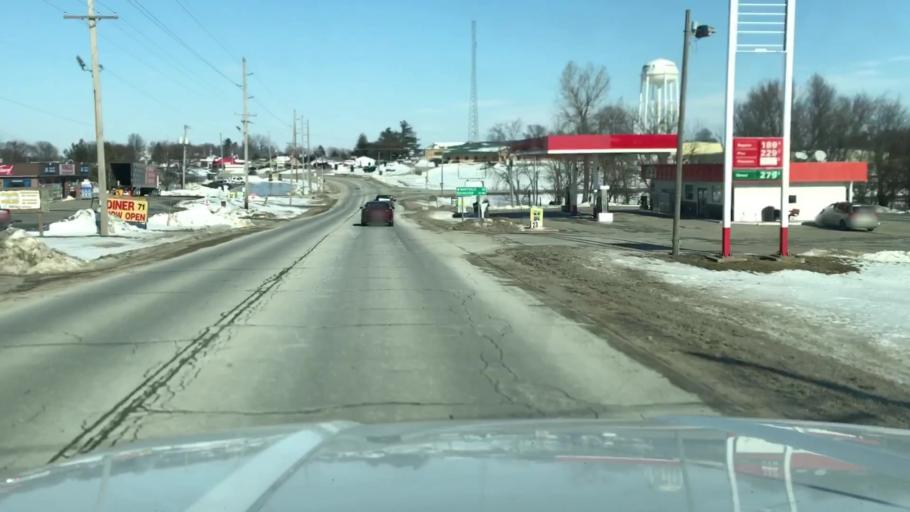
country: US
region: Missouri
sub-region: Andrew County
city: Savannah
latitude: 39.9432
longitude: -94.8219
